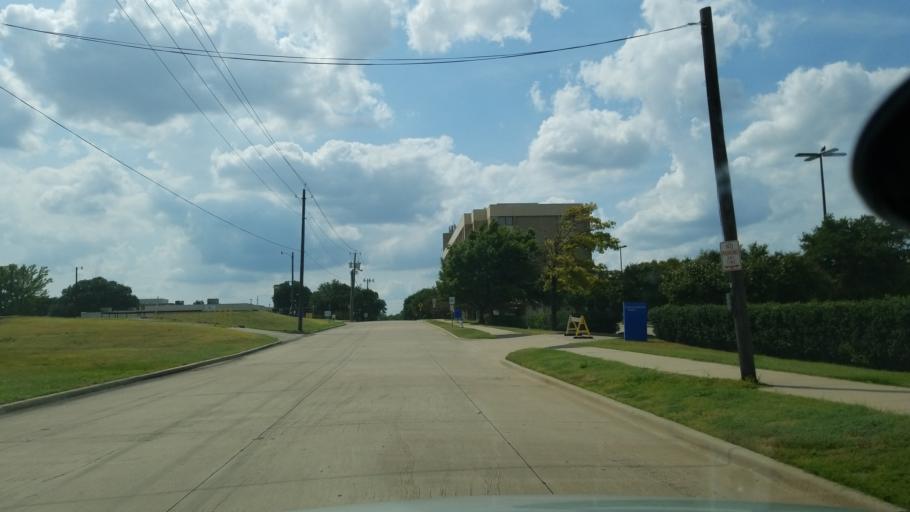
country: US
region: Texas
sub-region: Dallas County
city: Garland
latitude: 32.9186
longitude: -96.6595
